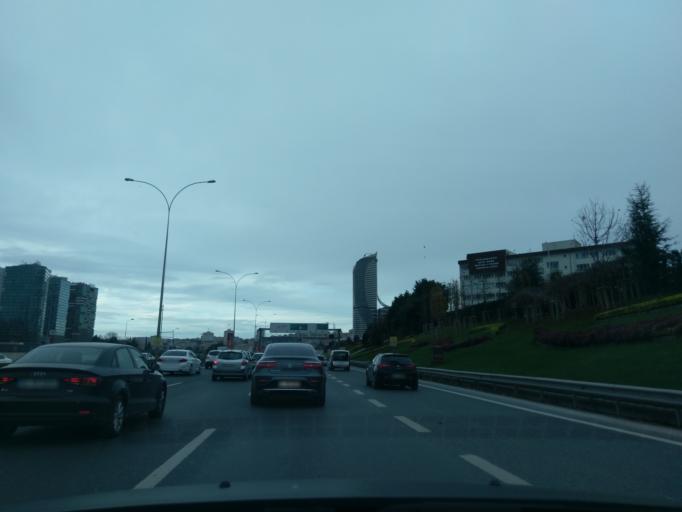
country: TR
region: Istanbul
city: UEskuedar
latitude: 40.9959
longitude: 29.0645
